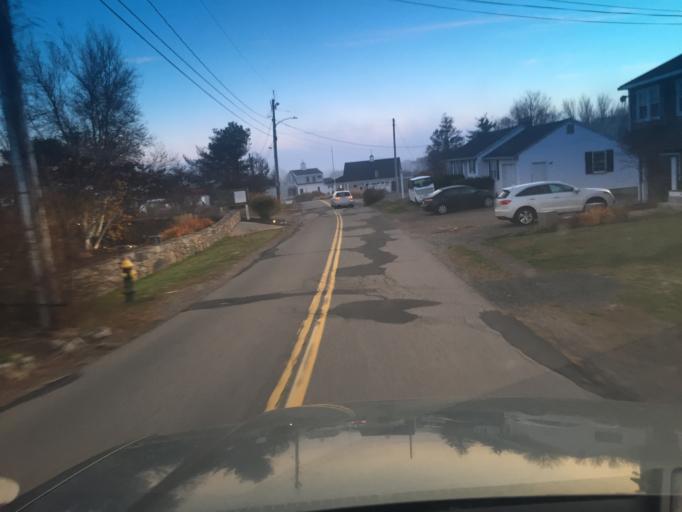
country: US
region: Maine
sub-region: York County
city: York Beach
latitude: 43.1689
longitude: -70.5956
